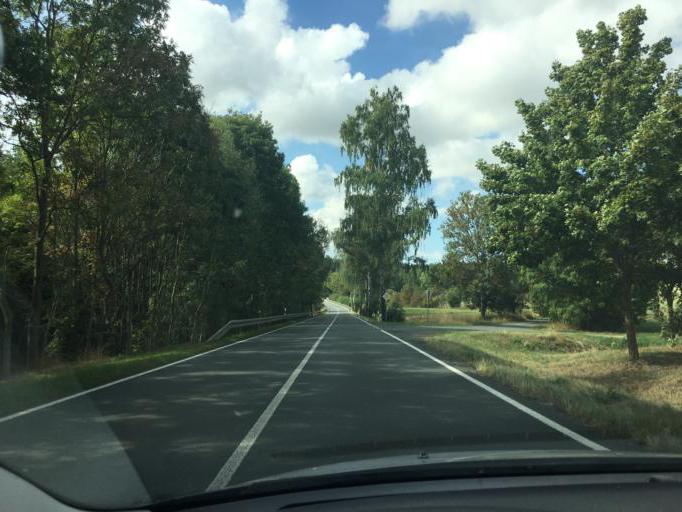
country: DE
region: Thuringia
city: Goschitz
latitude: 50.6372
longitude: 11.8457
